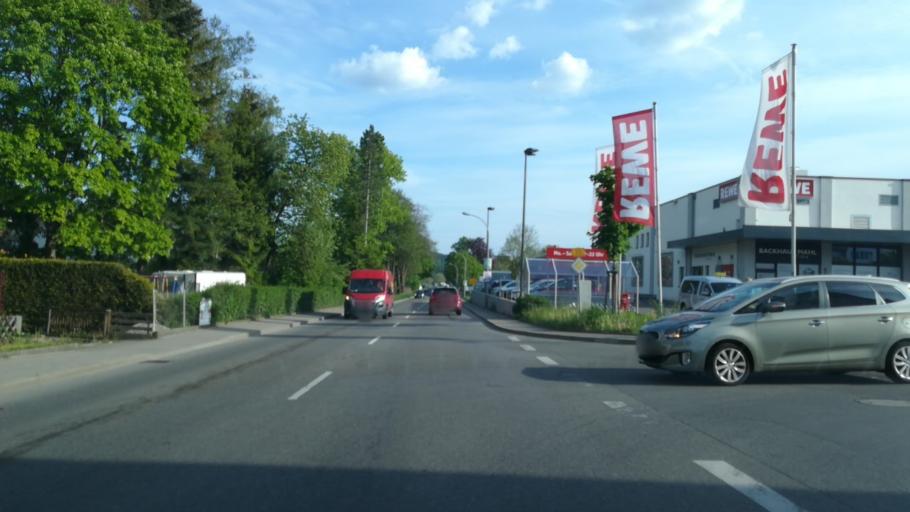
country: DE
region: Baden-Wuerttemberg
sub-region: Freiburg Region
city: Stockach
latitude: 47.8581
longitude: 9.0048
